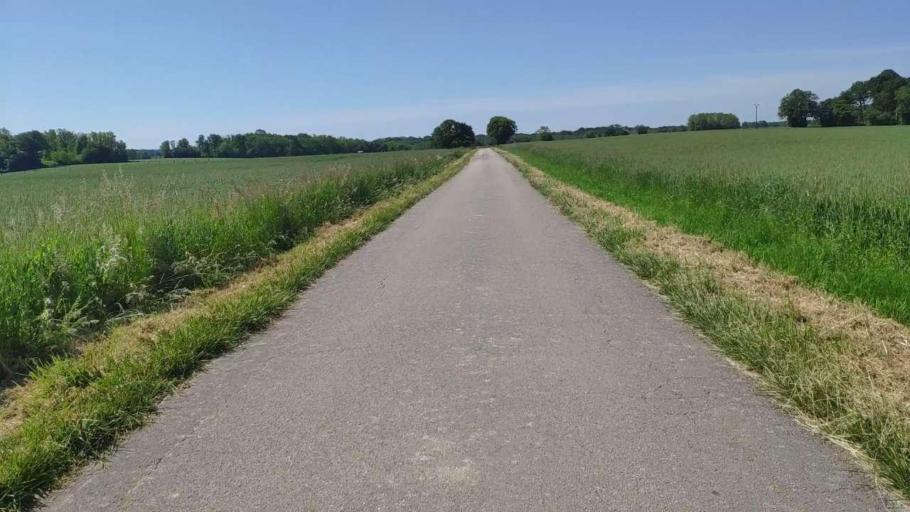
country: FR
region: Franche-Comte
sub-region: Departement du Jura
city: Bletterans
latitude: 46.7876
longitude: 5.4321
